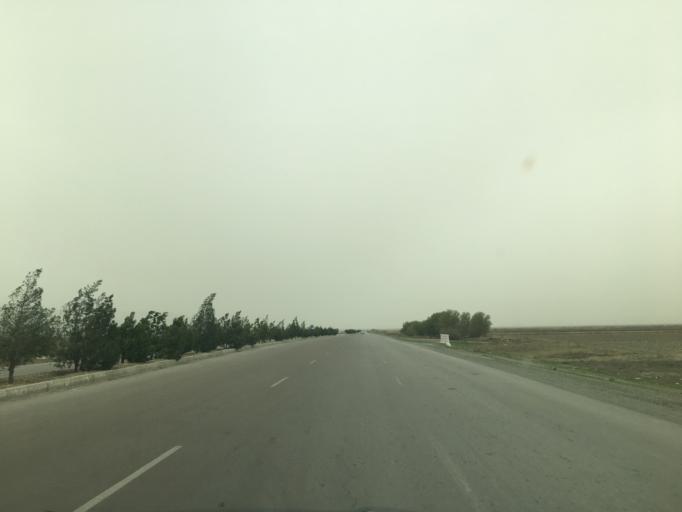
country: TM
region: Ahal
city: Baharly
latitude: 38.3467
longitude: 57.5549
